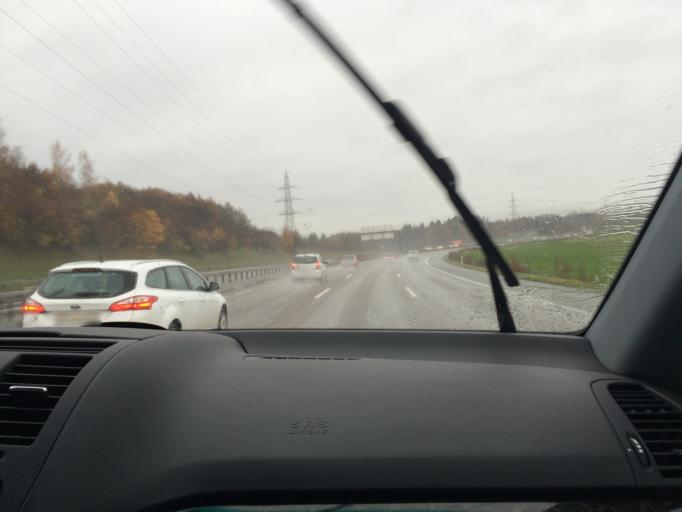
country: CH
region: Bern
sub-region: Bern-Mittelland District
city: Zollikofen
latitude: 46.9832
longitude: 7.4670
